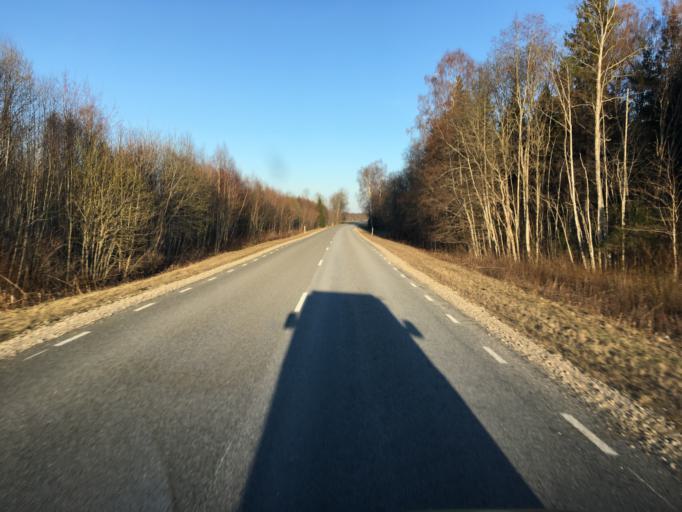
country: EE
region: Raplamaa
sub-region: Rapla vald
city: Rapla
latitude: 59.0753
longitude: 24.8797
